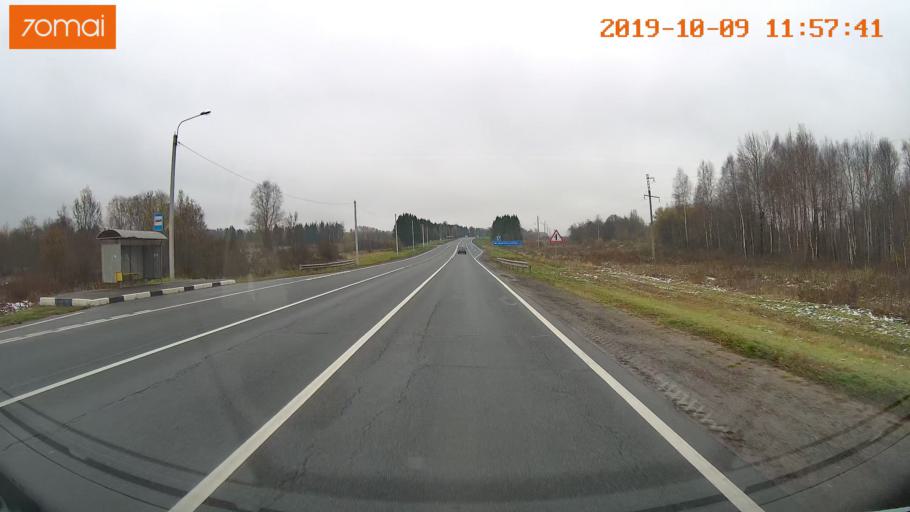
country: RU
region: Vologda
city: Gryazovets
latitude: 58.7288
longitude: 40.2940
